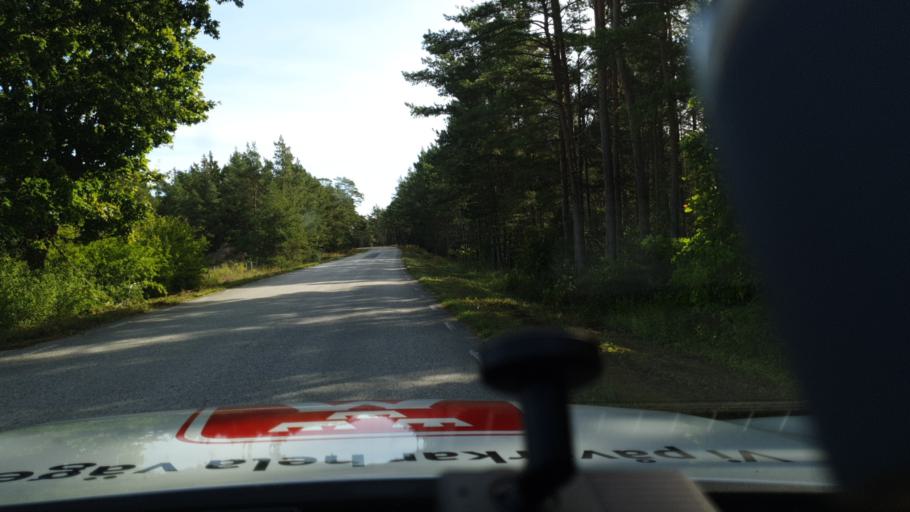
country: SE
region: Gotland
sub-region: Gotland
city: Slite
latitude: 57.8531
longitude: 18.7373
